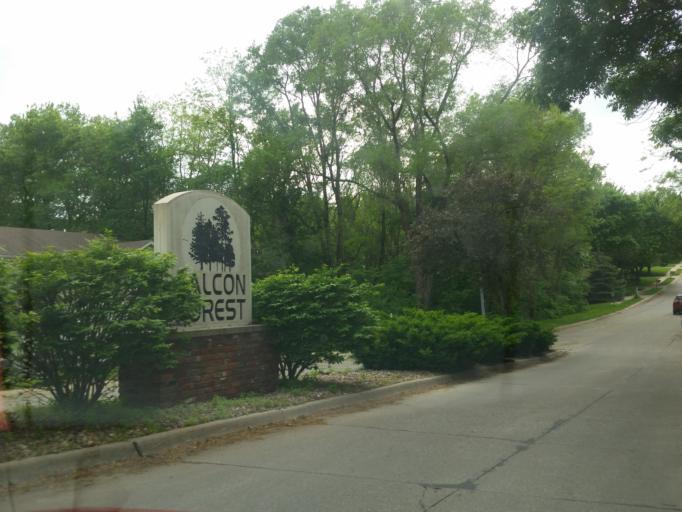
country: US
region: Nebraska
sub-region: Sarpy County
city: Offutt Air Force Base
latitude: 41.1114
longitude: -95.9667
